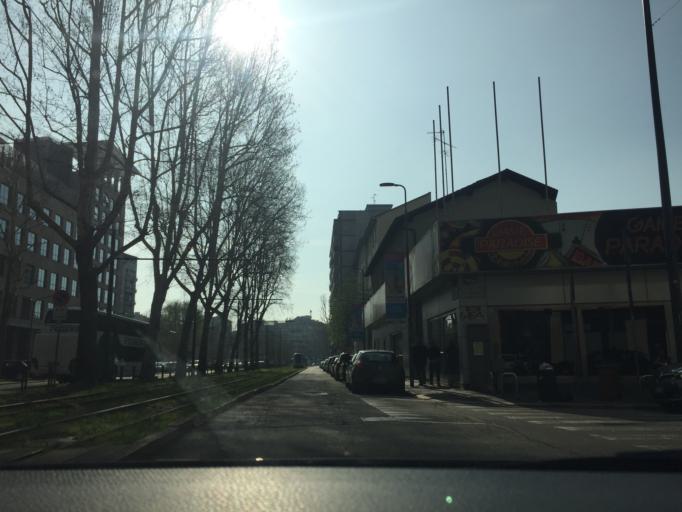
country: IT
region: Lombardy
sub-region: Citta metropolitana di Milano
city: Novate Milanese
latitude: 45.4892
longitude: 9.1533
